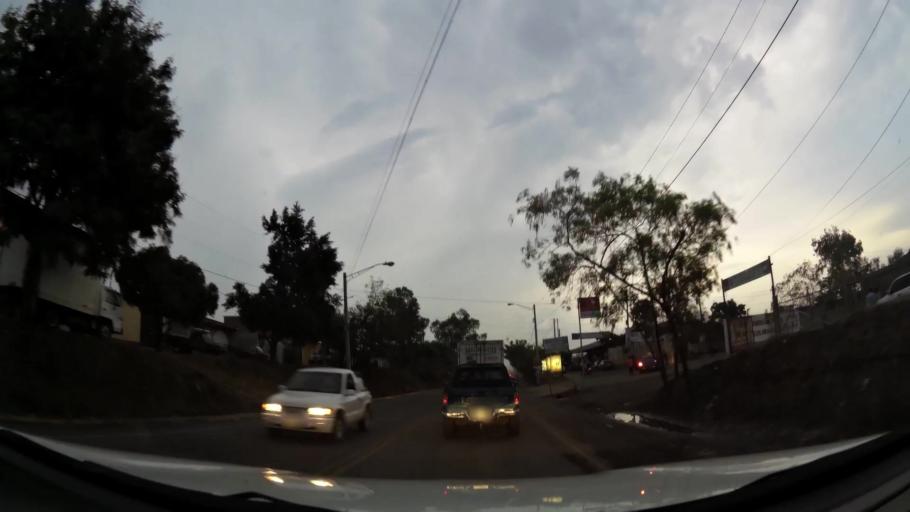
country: NI
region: Esteli
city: Esteli
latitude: 13.0755
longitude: -86.3526
